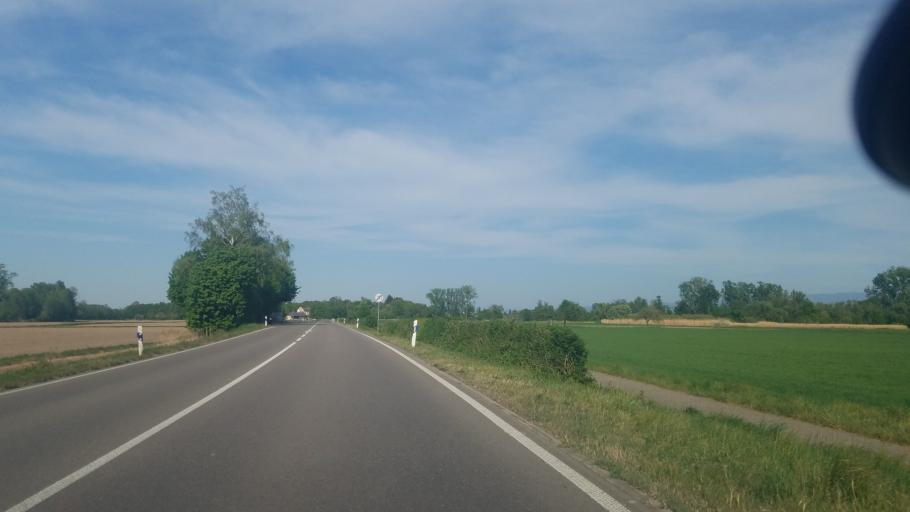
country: DE
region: Baden-Wuerttemberg
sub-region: Freiburg Region
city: Kehl
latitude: 48.5883
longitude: 7.8420
